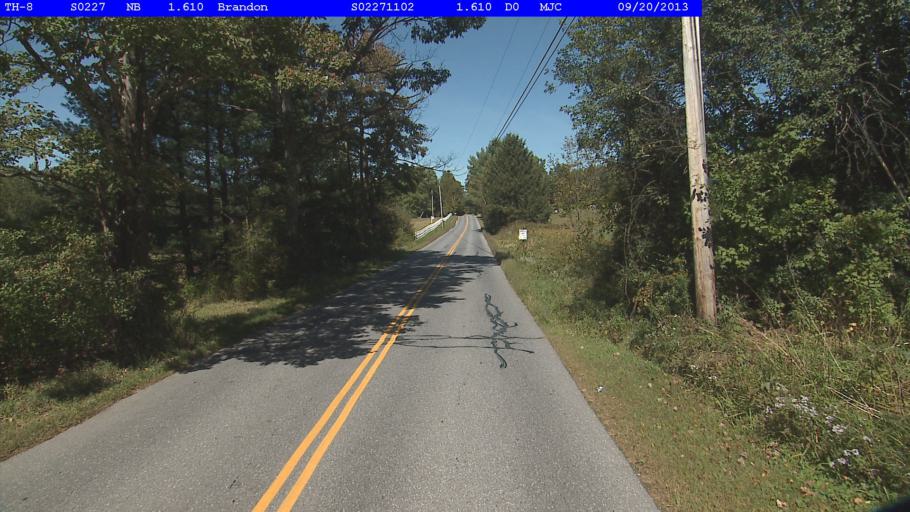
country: US
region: Vermont
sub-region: Rutland County
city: Brandon
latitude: 43.7976
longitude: -73.0549
